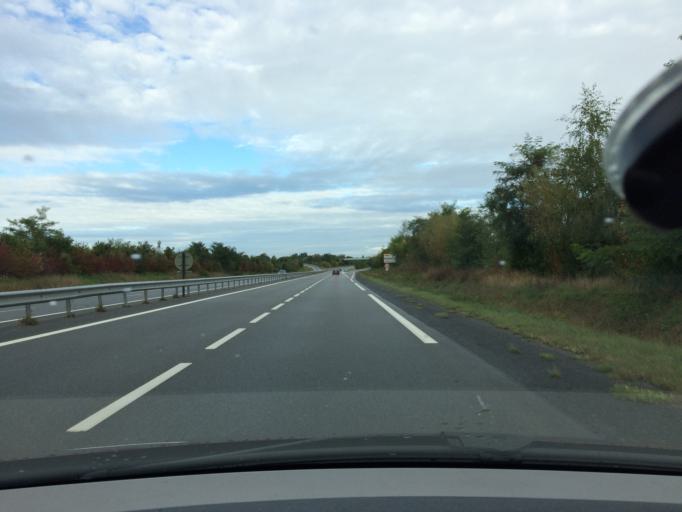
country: FR
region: Brittany
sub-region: Departement d'Ille-et-Vilaine
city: Corps-Nuds
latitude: 47.9770
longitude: -1.5535
